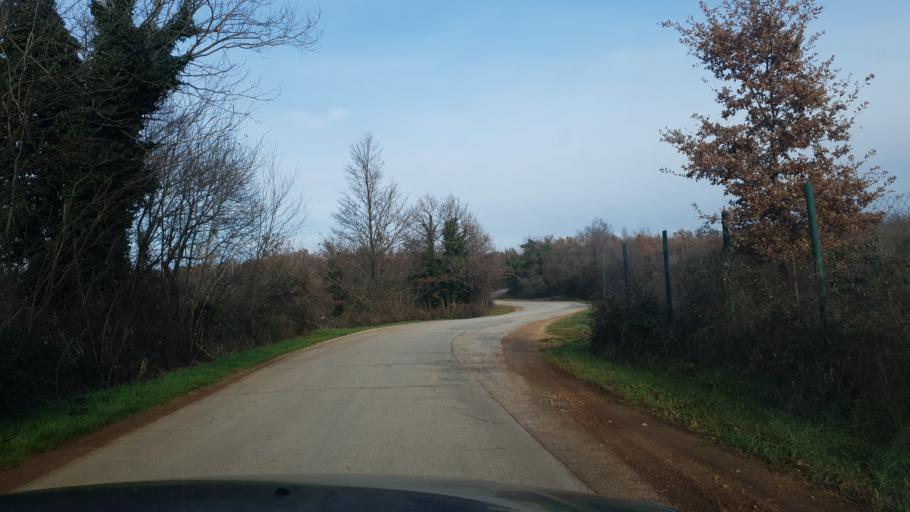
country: HR
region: Istarska
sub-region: Grad Porec
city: Porec
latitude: 45.2366
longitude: 13.6365
